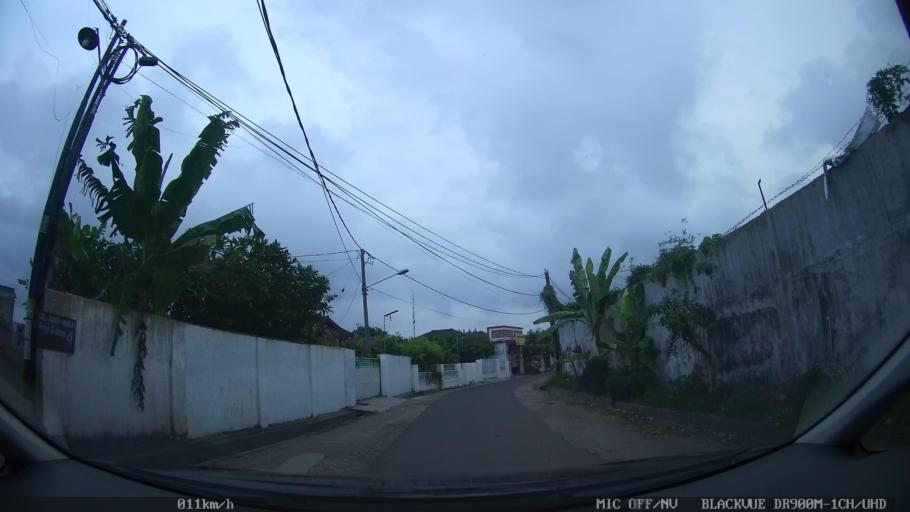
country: ID
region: Lampung
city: Bandarlampung
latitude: -5.4058
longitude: 105.2801
